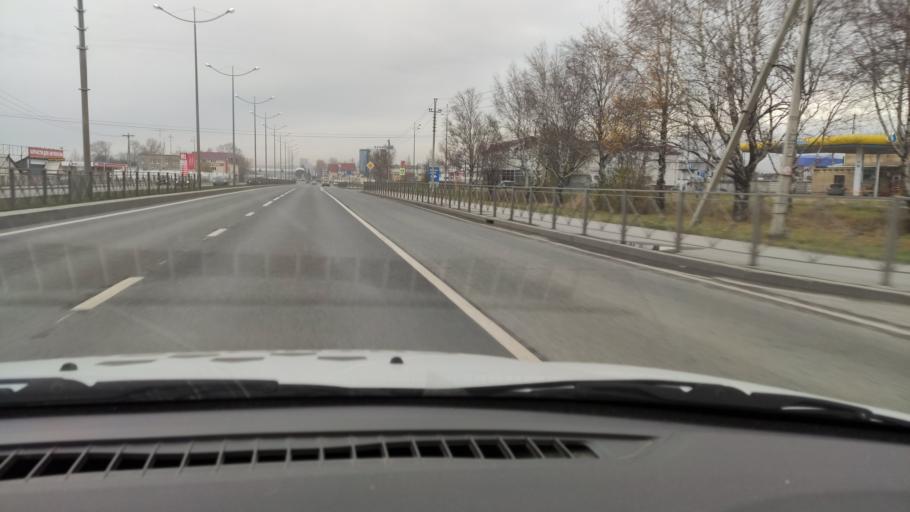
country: RU
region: Perm
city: Kondratovo
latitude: 57.9498
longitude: 56.1023
